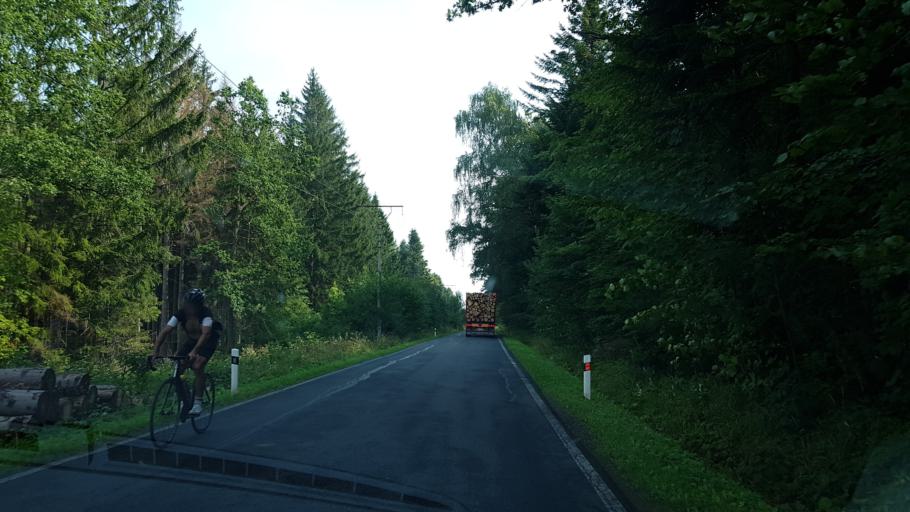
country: CZ
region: Olomoucky
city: Zlate Hory
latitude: 50.2522
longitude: 17.3723
